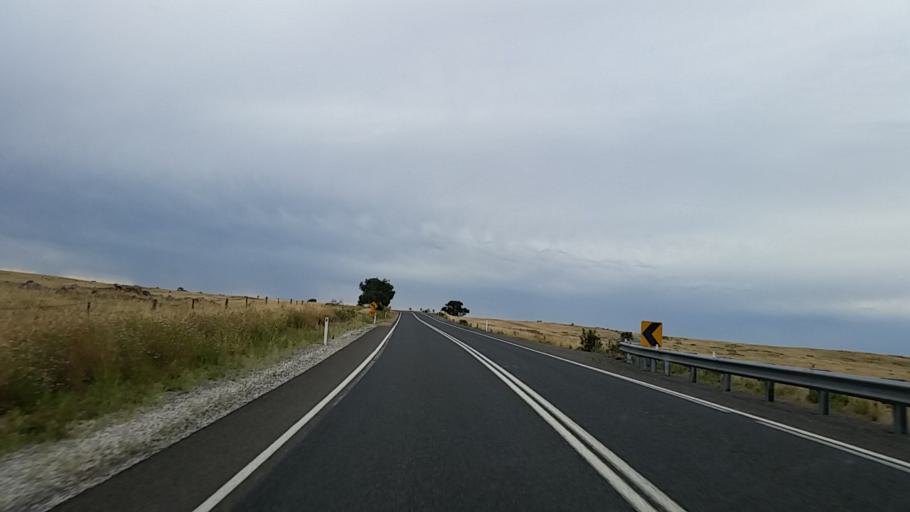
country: AU
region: South Australia
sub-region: Mid Murray
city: Mannum
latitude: -34.7566
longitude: 139.1727
